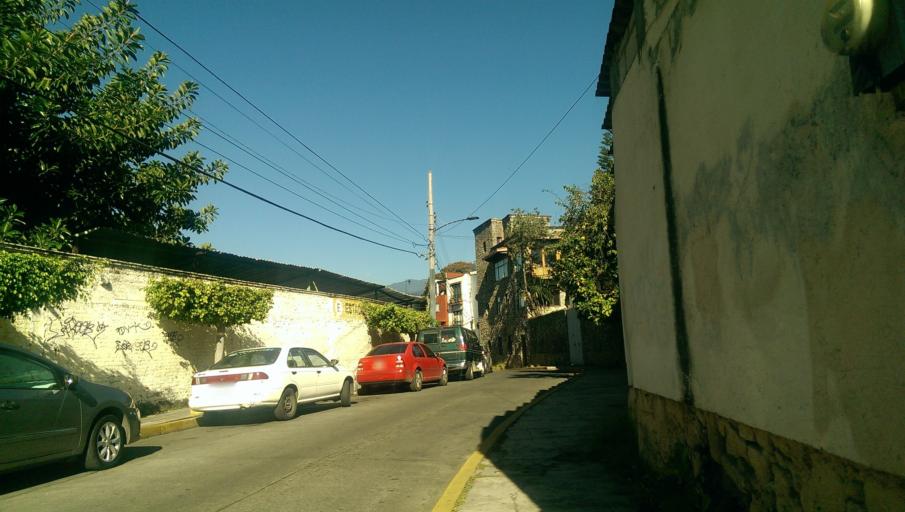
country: MX
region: Morelos
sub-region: Cuernavaca
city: Cuernavaca
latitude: 18.9223
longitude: -99.2382
